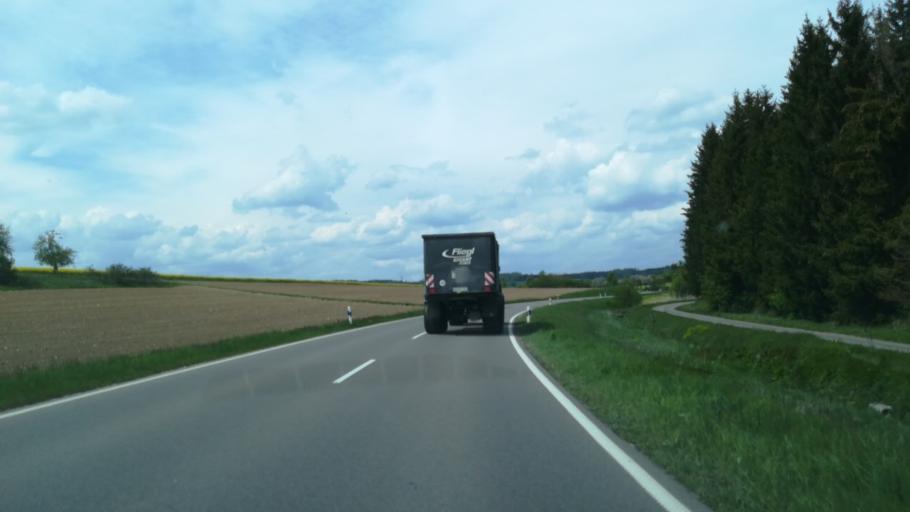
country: DE
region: Baden-Wuerttemberg
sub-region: Tuebingen Region
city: Messkirch
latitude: 48.0133
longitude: 9.1117
